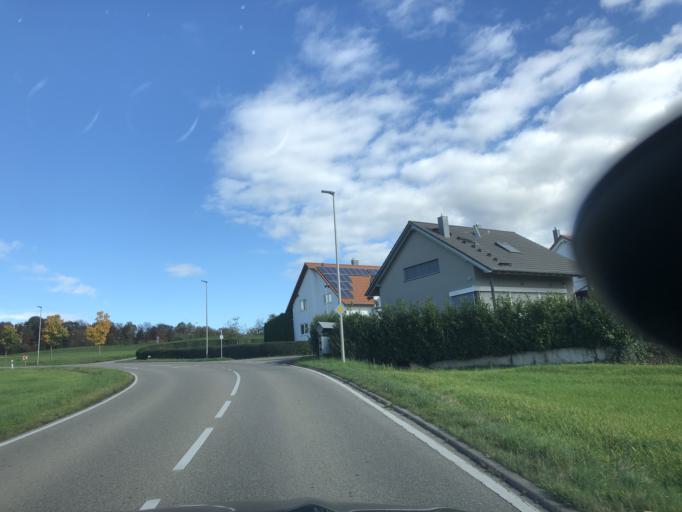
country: DE
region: Baden-Wuerttemberg
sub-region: Regierungsbezirk Stuttgart
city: Allmersbach im Tal
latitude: 48.8886
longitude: 9.4606
